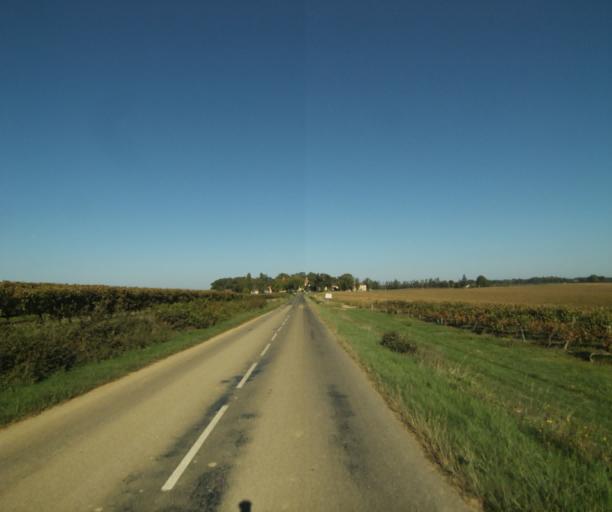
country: FR
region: Aquitaine
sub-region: Departement des Landes
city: Gabarret
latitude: 43.9175
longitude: 0.0194
